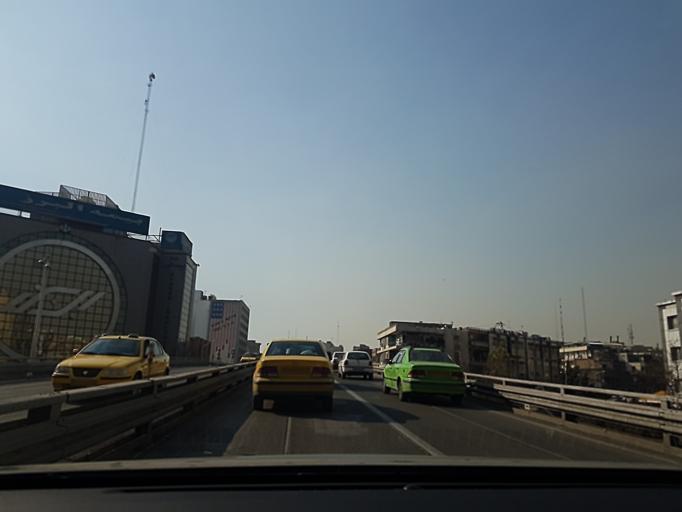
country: IR
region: Tehran
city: Tehran
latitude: 35.7153
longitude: 51.4180
